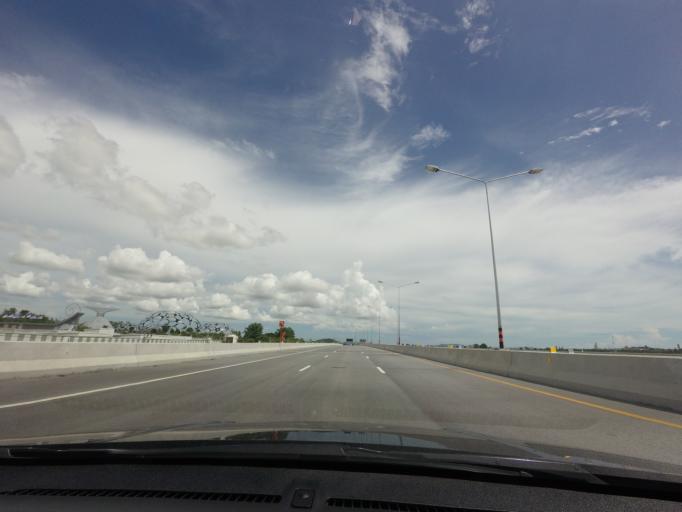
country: TH
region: Chon Buri
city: Phatthaya
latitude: 12.9202
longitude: 100.9535
